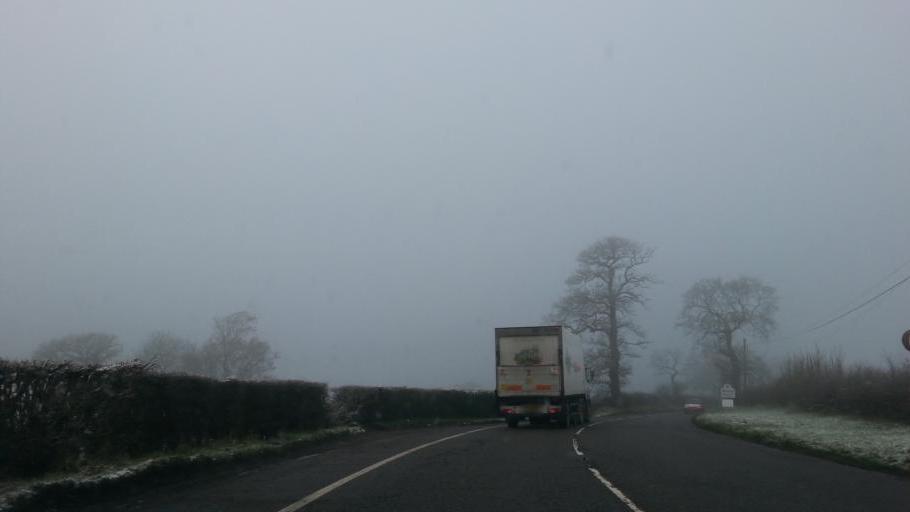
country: GB
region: England
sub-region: Cheshire East
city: Eaton
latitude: 53.1949
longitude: -2.2211
